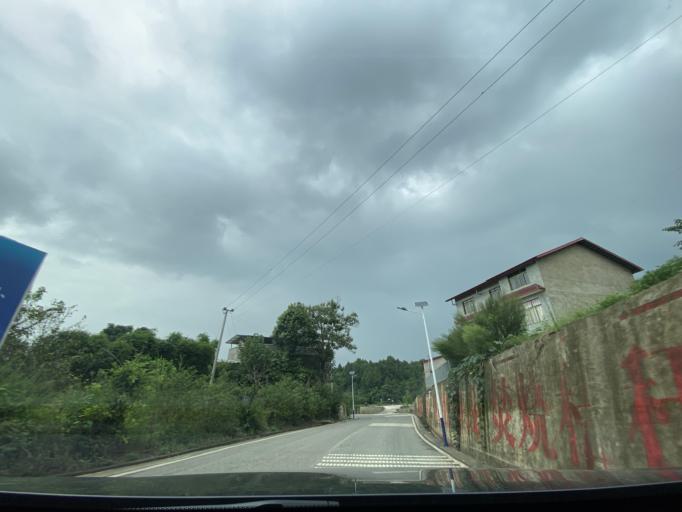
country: CN
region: Sichuan
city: Jiancheng
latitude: 30.5424
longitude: 104.5194
